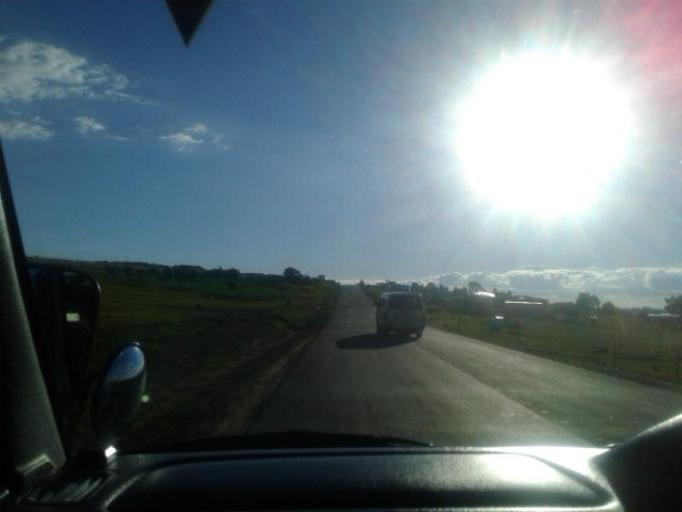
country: LS
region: Maseru
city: Maseru
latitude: -29.3125
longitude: 27.5958
